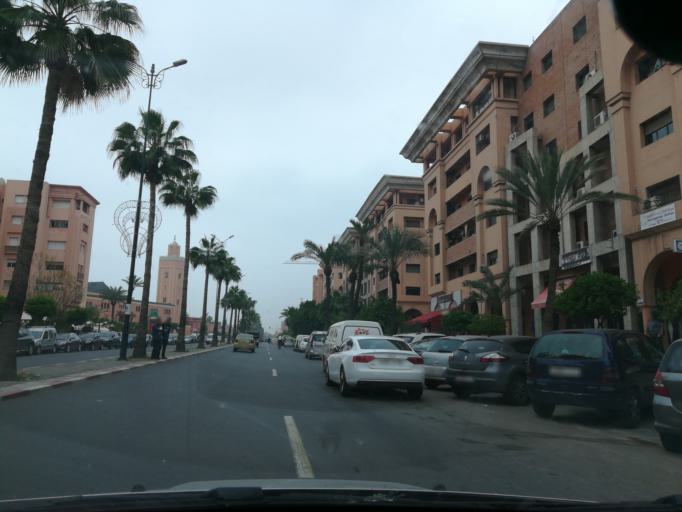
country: MA
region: Marrakech-Tensift-Al Haouz
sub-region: Marrakech
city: Marrakesh
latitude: 31.6582
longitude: -8.0052
